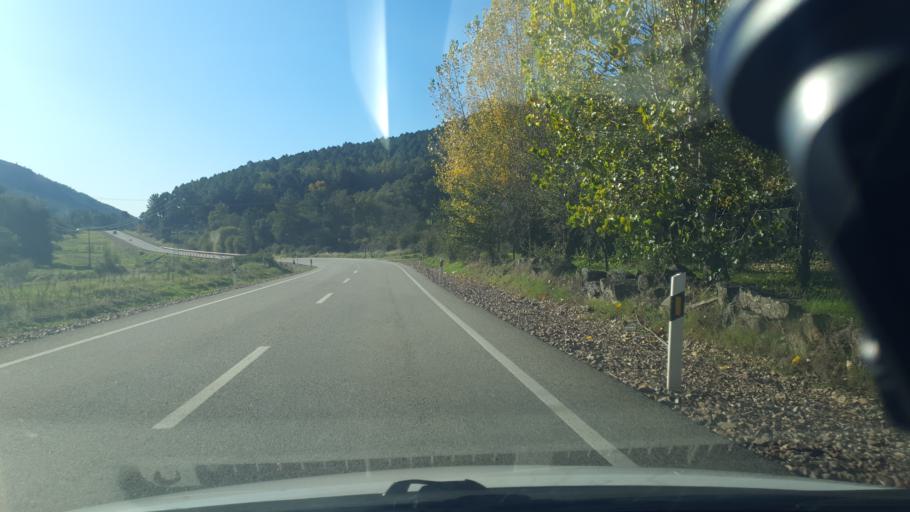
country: ES
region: Castille and Leon
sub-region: Provincia de Avila
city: Mombeltran
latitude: 40.2304
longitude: -5.0340
